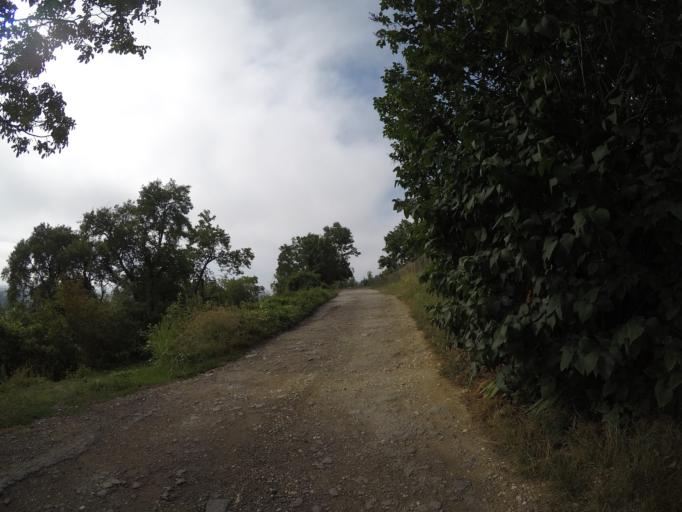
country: SK
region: Trenciansky
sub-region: Okres Nove Mesto nad Vahom
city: Nove Mesto nad Vahom
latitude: 48.7620
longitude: 17.8163
